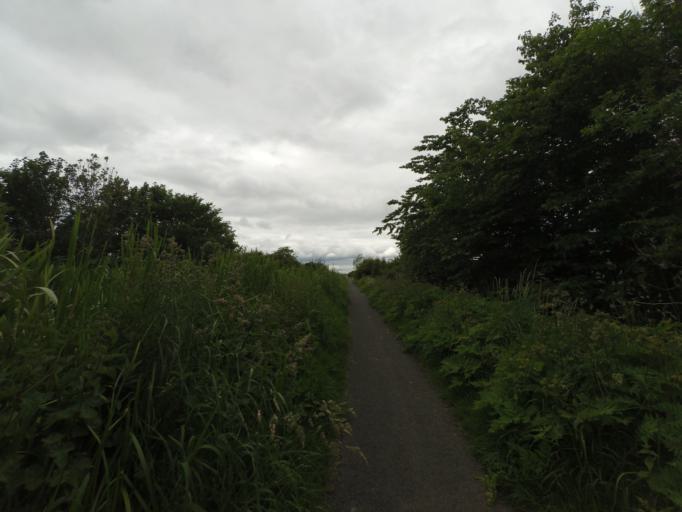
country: GB
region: Scotland
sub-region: West Lothian
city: Broxburn
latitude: 55.9755
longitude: -3.5251
